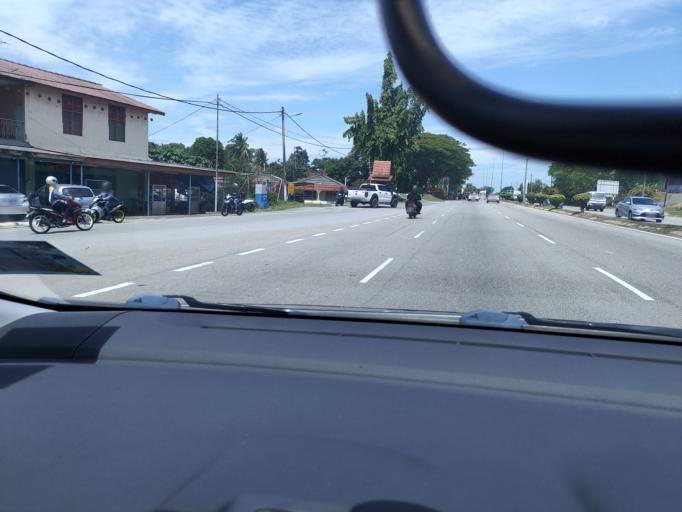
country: MY
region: Melaka
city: Batu Berendam
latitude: 2.2634
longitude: 102.2194
